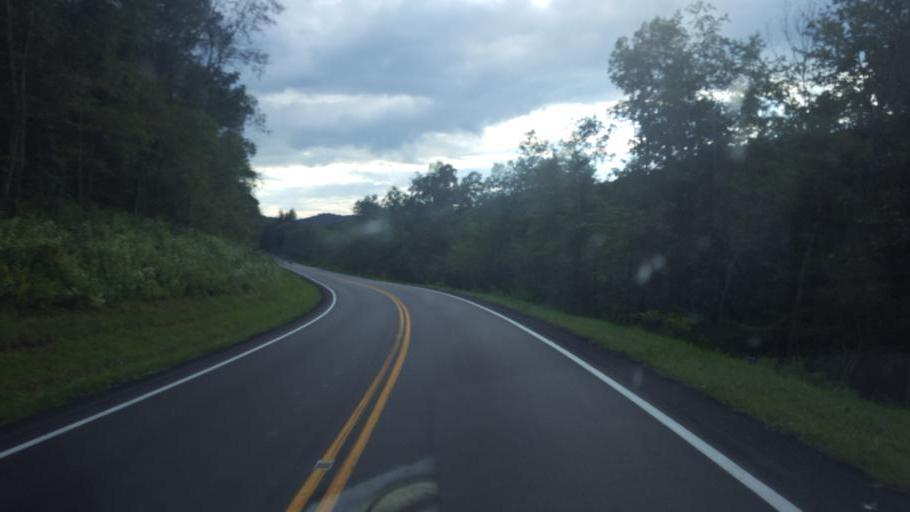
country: US
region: Ohio
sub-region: Knox County
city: Oak Hill
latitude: 40.4662
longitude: -82.1520
